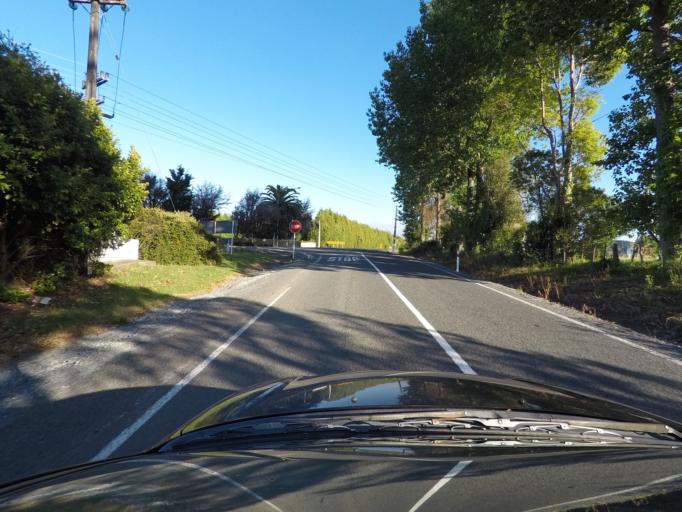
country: NZ
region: Northland
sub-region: Whangarei
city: Whangarei
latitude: -35.6400
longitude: 174.2972
